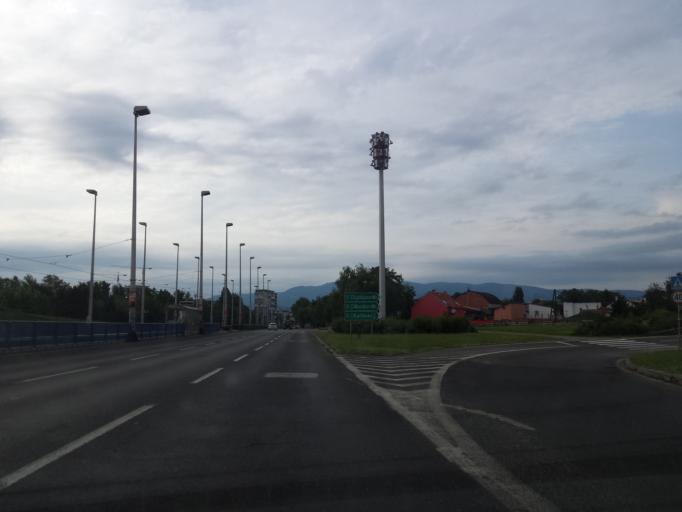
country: HR
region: Grad Zagreb
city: Novi Zagreb
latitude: 45.7962
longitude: 15.9994
